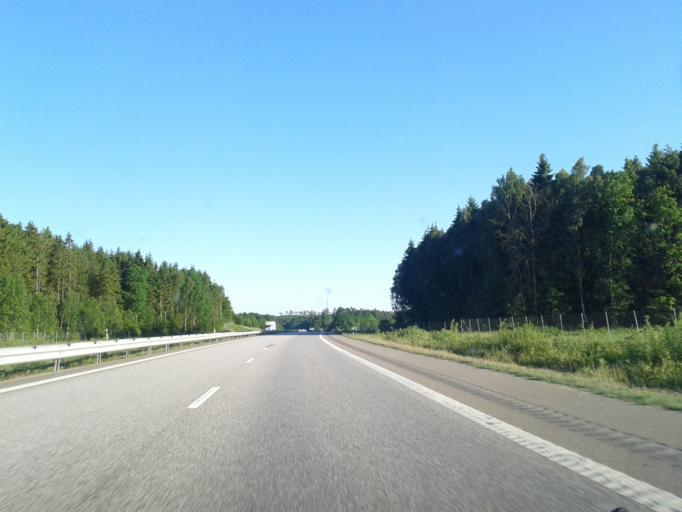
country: SE
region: Vaestra Goetaland
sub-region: Uddevalla Kommun
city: Uddevalla
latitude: 58.3124
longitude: 11.8589
